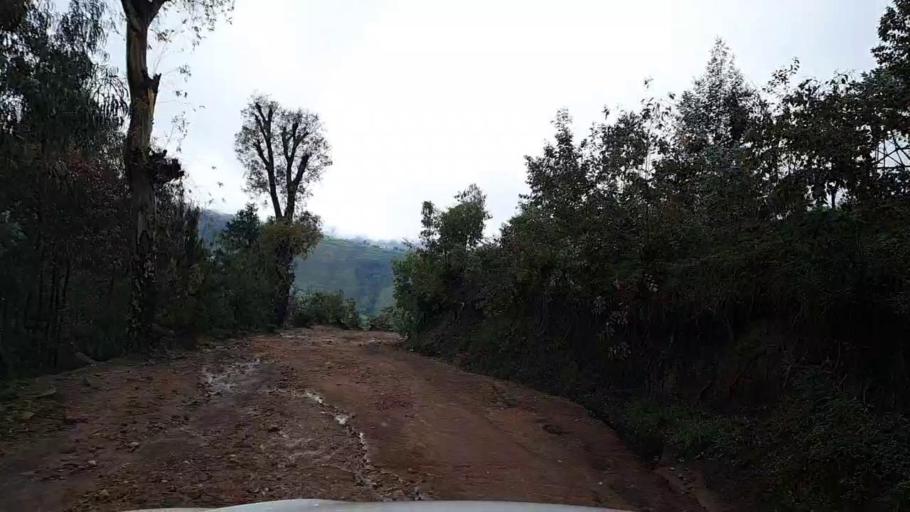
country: RW
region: Southern Province
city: Nzega
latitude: -2.3948
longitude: 29.4981
